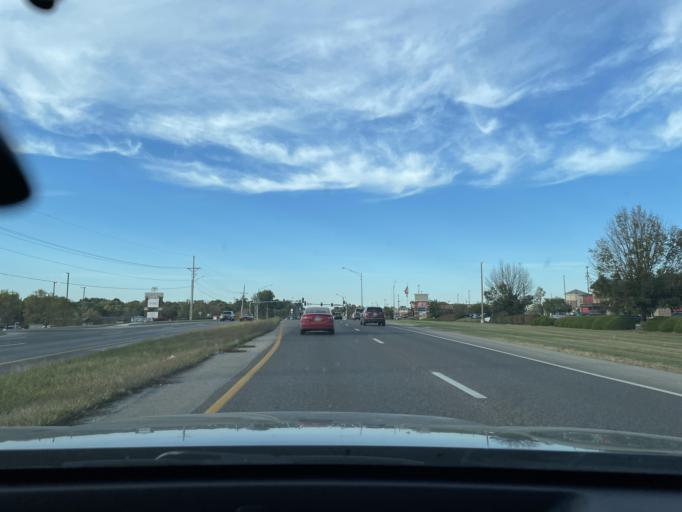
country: US
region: Missouri
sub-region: Andrew County
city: Country Club Village
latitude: 39.8124
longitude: -94.8151
